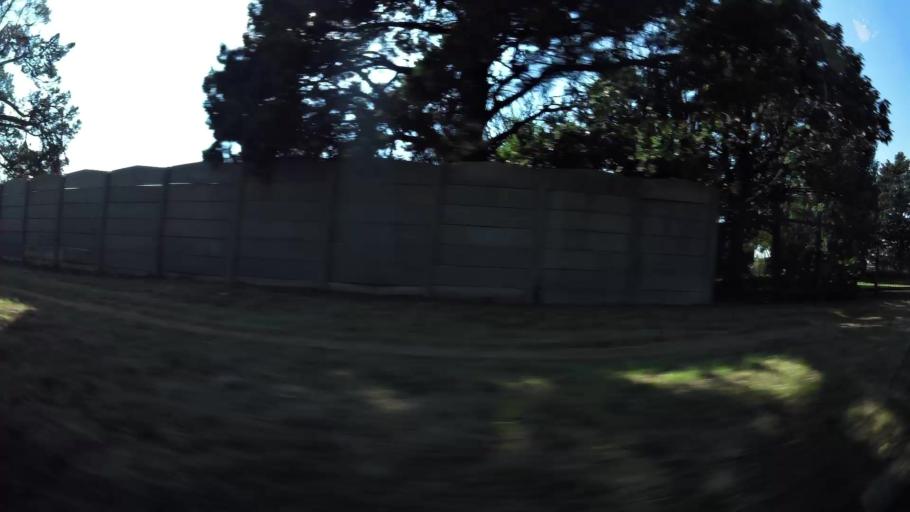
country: ZA
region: Gauteng
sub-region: Ekurhuleni Metropolitan Municipality
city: Benoni
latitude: -26.1491
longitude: 28.3151
